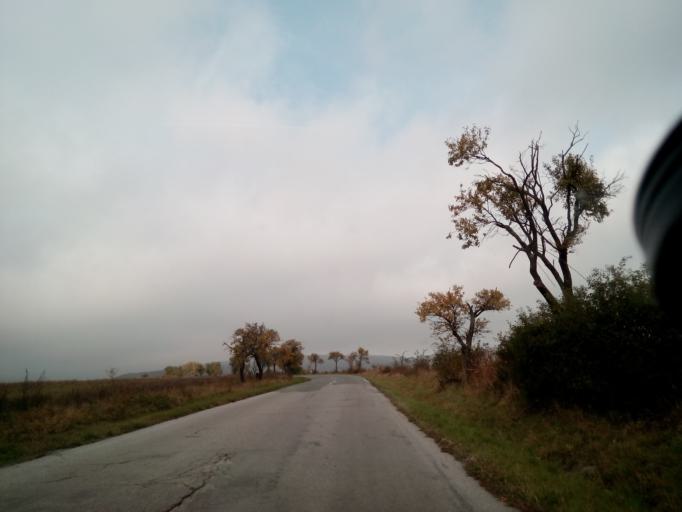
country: SK
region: Kosicky
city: Kosice
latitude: 48.7341
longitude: 21.1294
